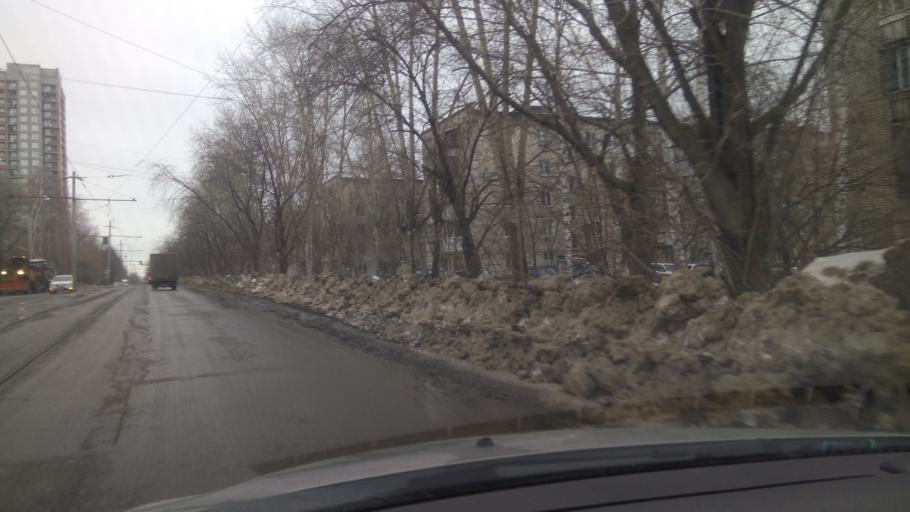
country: RU
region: Sverdlovsk
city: Yekaterinburg
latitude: 56.8974
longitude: 60.6354
